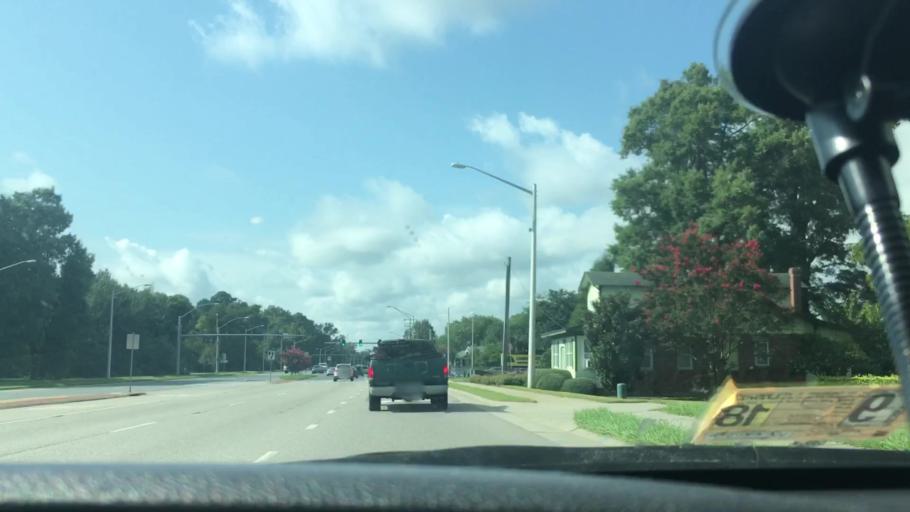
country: US
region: Virginia
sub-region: City of Virginia Beach
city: Virginia Beach
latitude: 36.8399
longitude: -76.0491
